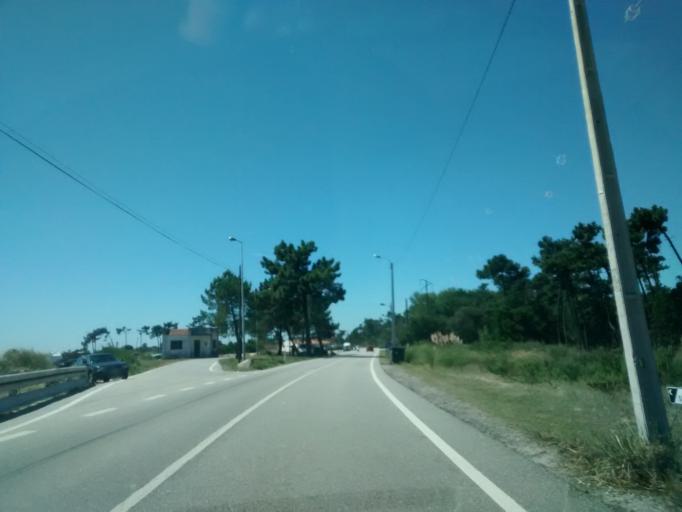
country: PT
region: Aveiro
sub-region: Ilhavo
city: Gafanha da Nazare
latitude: 40.6725
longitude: -8.7228
